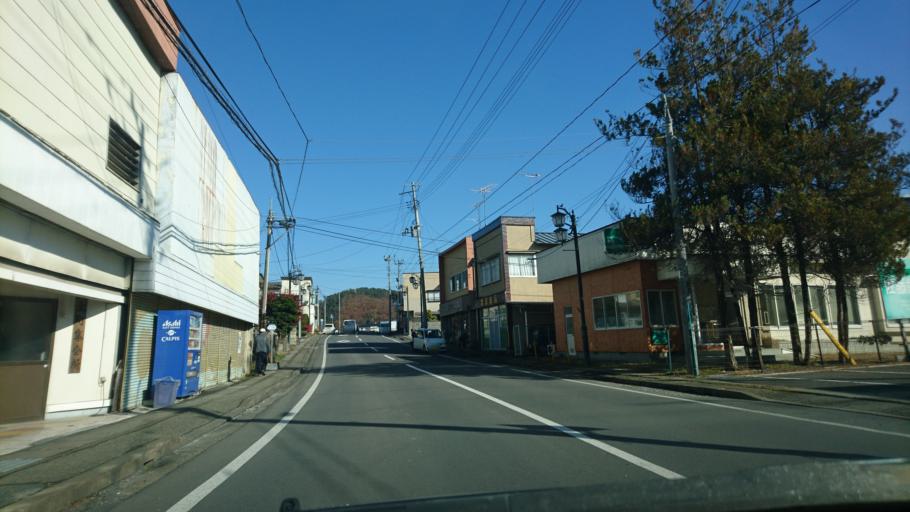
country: JP
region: Iwate
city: Ichinoseki
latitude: 38.9926
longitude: 141.2522
